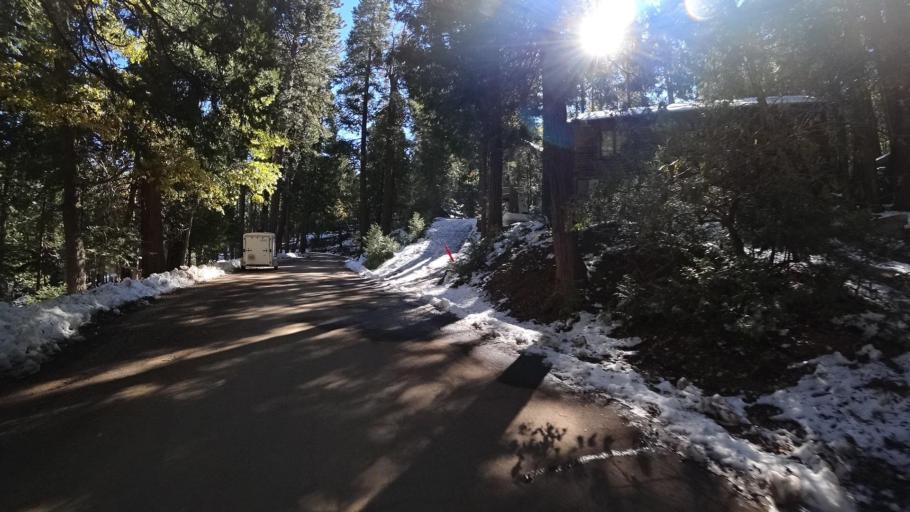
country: US
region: California
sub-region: Kern County
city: Alta Sierra
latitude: 35.7269
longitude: -118.5513
